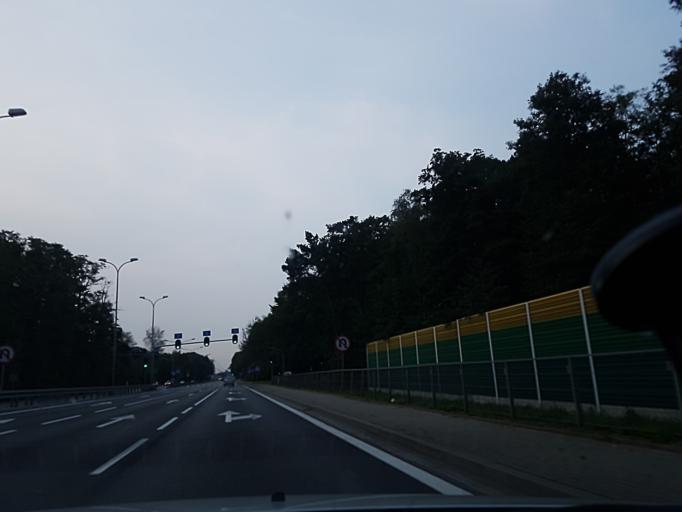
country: PL
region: Lodz Voivodeship
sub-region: Powiat lodzki wschodni
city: Tuszyn
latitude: 51.6178
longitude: 19.5210
